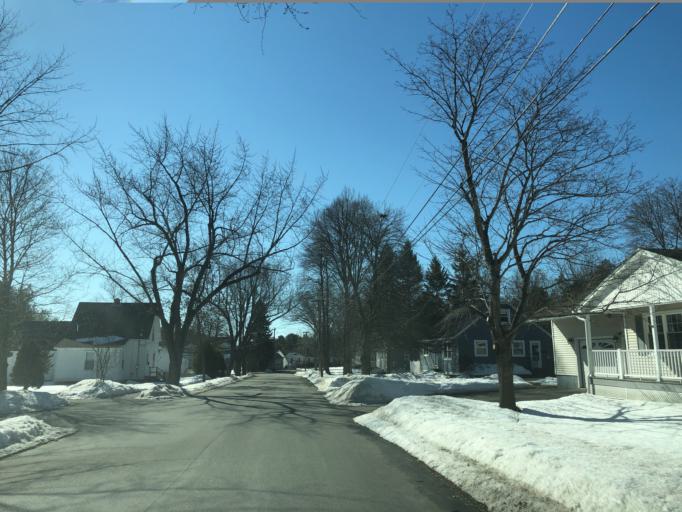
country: US
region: Maine
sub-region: Penobscot County
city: Brewer
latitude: 44.8181
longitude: -68.7533
